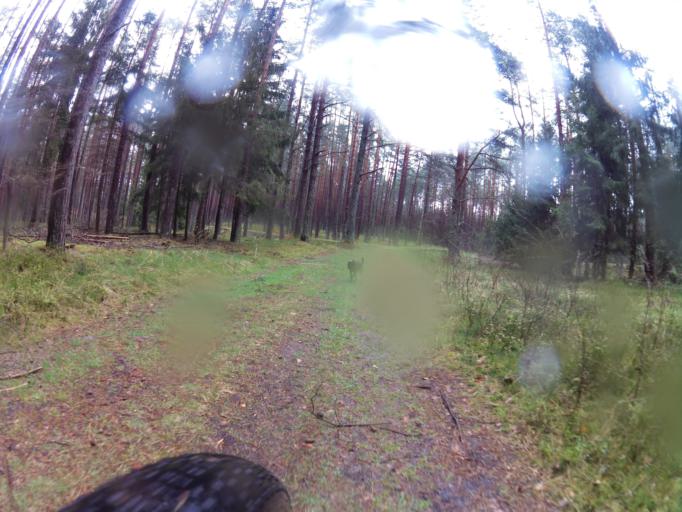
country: PL
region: Pomeranian Voivodeship
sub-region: Powiat slupski
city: Kepice
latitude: 54.2410
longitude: 16.7849
